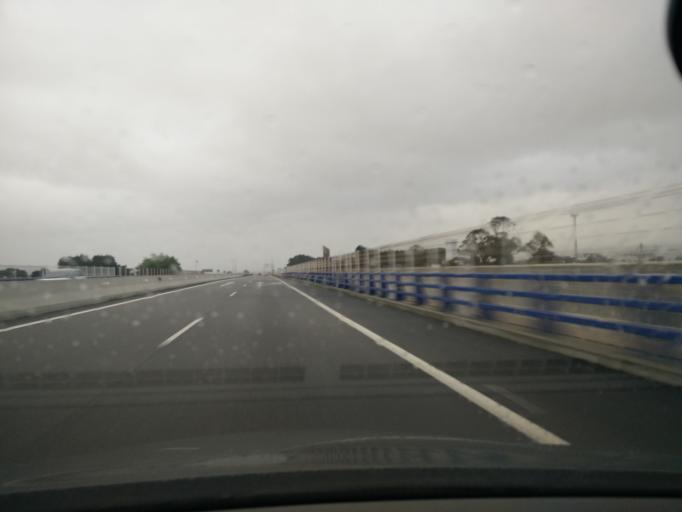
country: ES
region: Asturias
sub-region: Province of Asturias
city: Figueras
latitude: 43.5429
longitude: -7.0323
